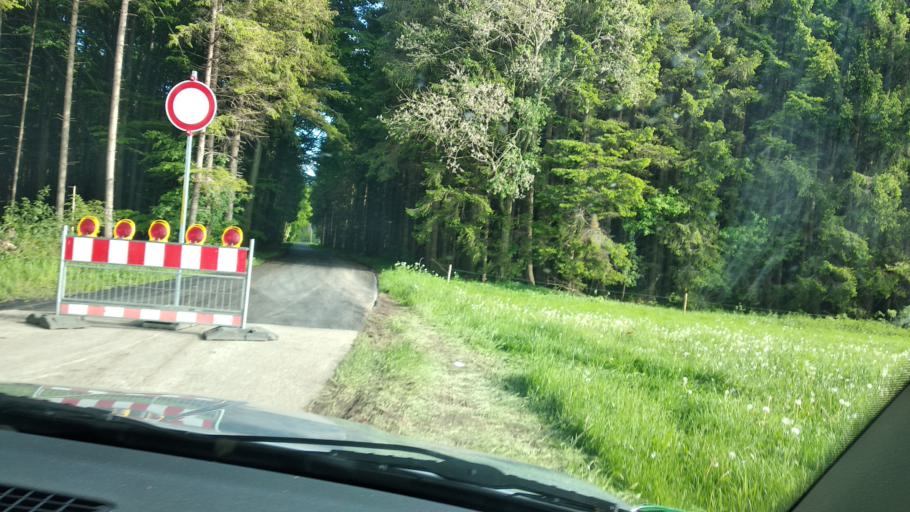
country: DE
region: Bavaria
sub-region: Swabia
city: Kronburg
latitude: 47.8813
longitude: 10.1490
